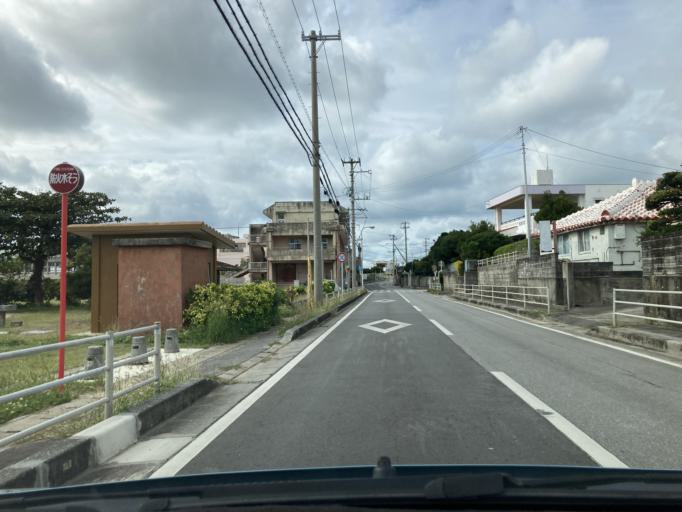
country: JP
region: Okinawa
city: Itoman
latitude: 26.1035
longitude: 127.6914
